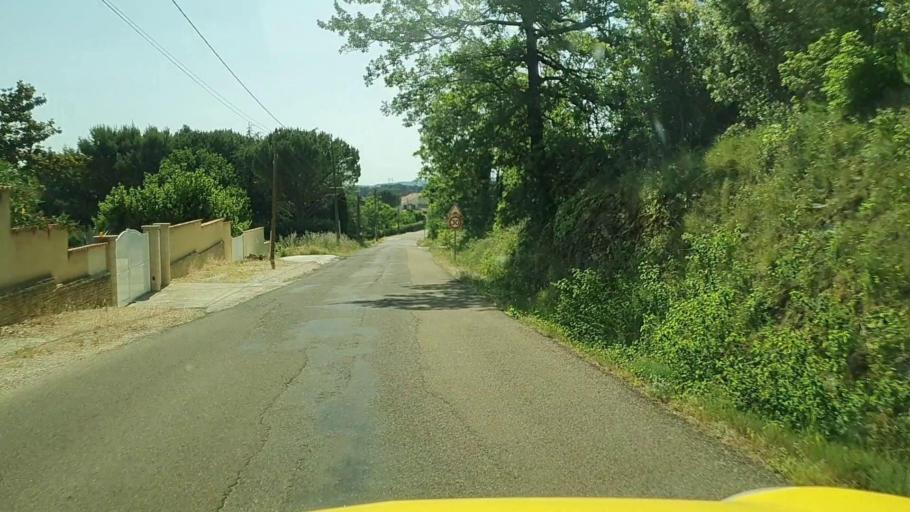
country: FR
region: Languedoc-Roussillon
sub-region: Departement du Gard
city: Connaux
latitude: 44.0902
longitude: 4.5888
